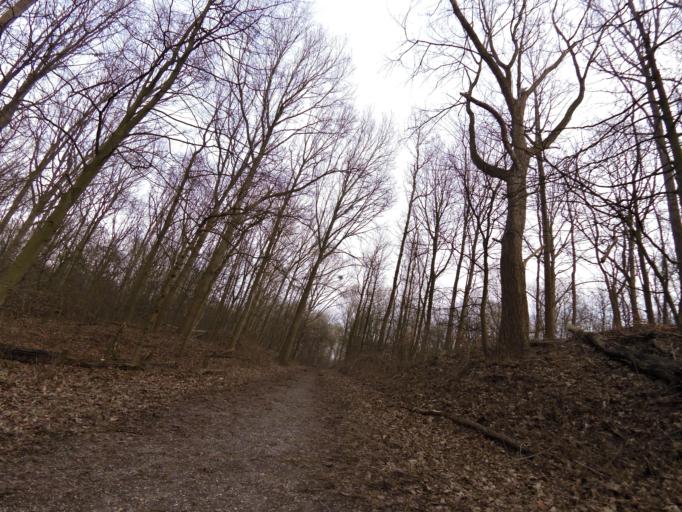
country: NL
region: South Holland
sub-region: Gemeente Hellevoetsluis
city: Nieuw-Helvoet
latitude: 51.9087
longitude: 4.0651
